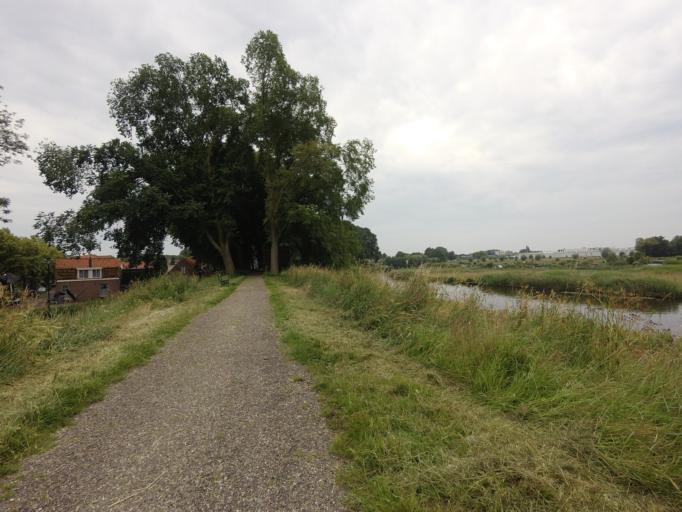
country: NL
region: North Holland
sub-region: Gemeente Enkhuizen
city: Enkhuizen
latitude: 52.7039
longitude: 5.2777
